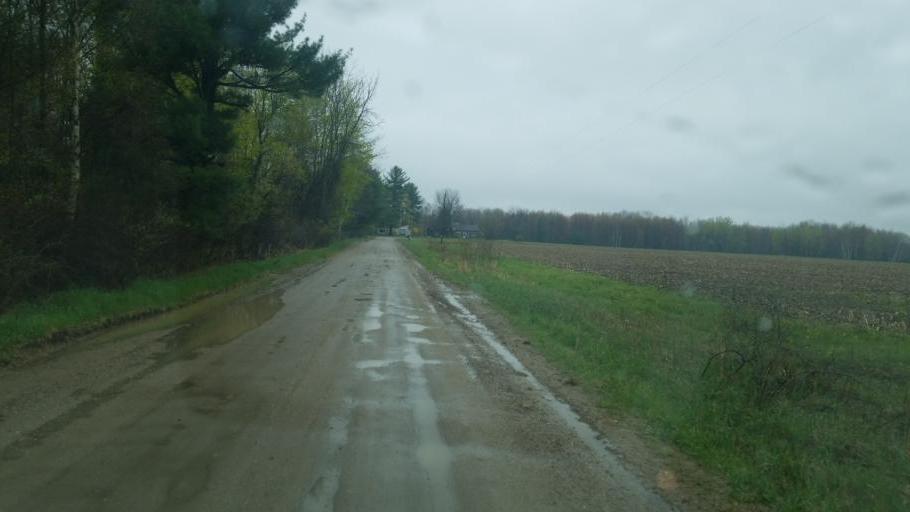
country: US
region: Michigan
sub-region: Montcalm County
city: Lakeview
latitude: 43.4657
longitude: -85.3133
